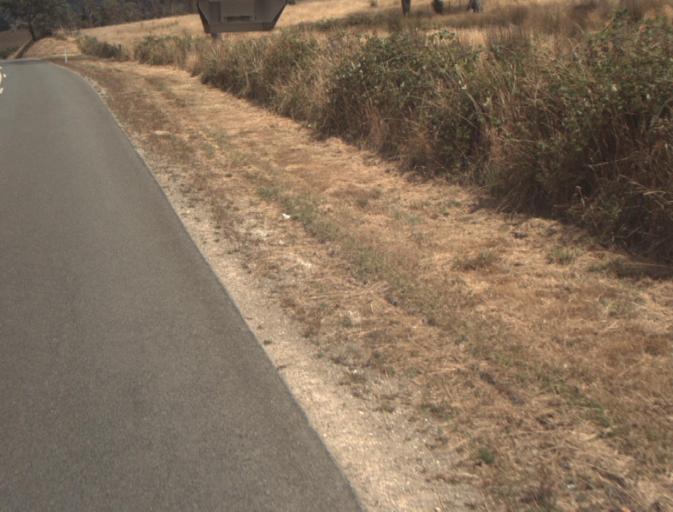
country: AU
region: Tasmania
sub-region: Launceston
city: Mayfield
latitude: -41.2191
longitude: 147.1215
